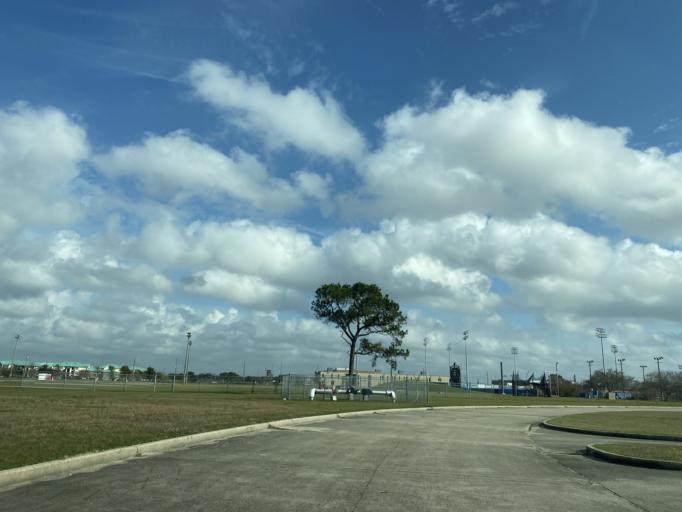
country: US
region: Louisiana
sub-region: Orleans Parish
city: New Orleans
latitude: 30.0321
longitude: -90.0500
